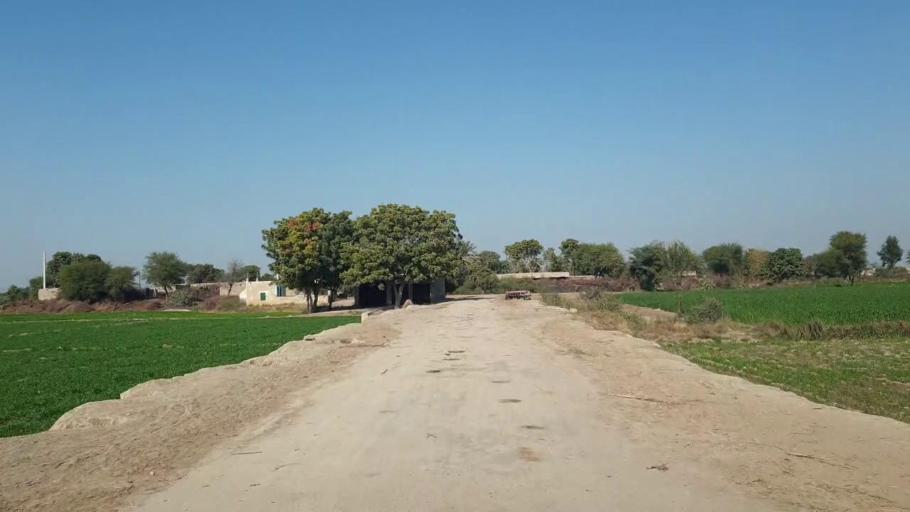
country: PK
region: Sindh
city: Shahdadpur
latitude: 25.9612
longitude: 68.6406
